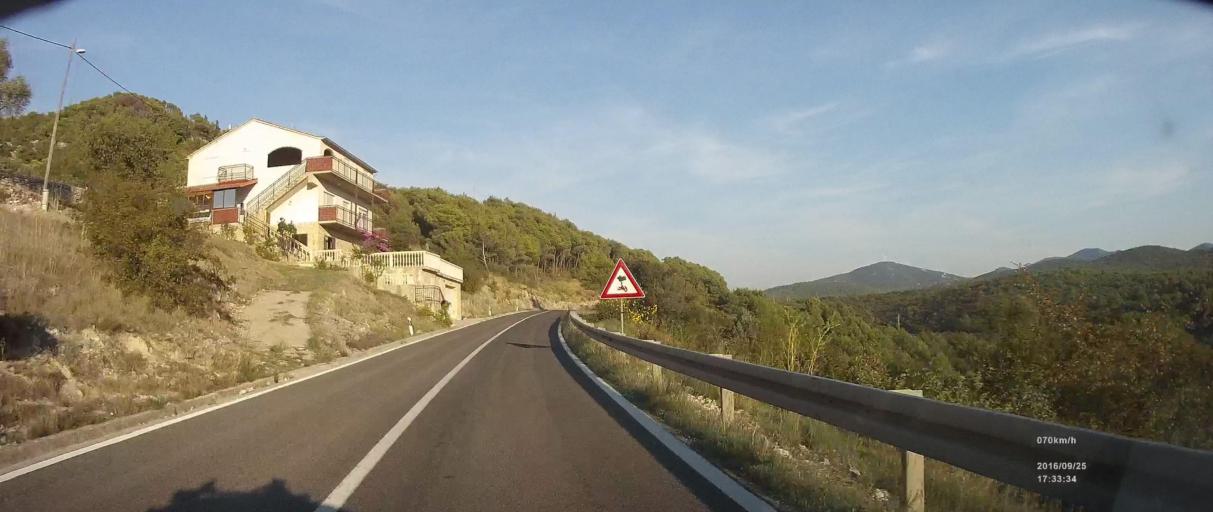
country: HR
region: Sibensko-Kniniska
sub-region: Grad Sibenik
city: Brodarica
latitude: 43.6755
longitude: 16.0148
